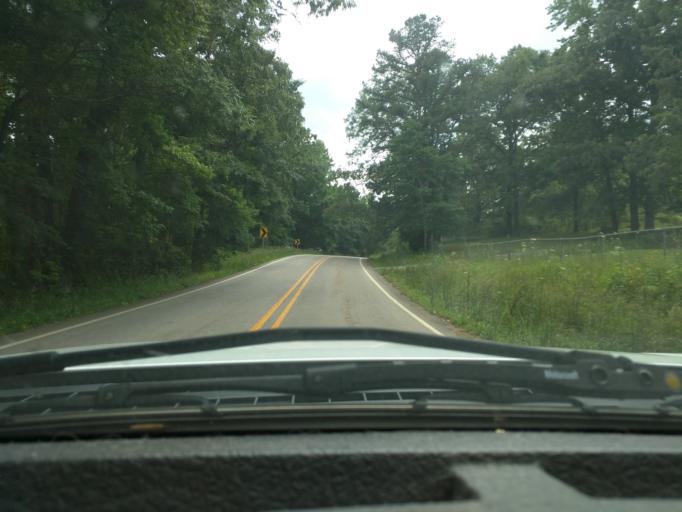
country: US
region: Arkansas
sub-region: Franklin County
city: Ozark
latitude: 35.6768
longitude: -93.8302
